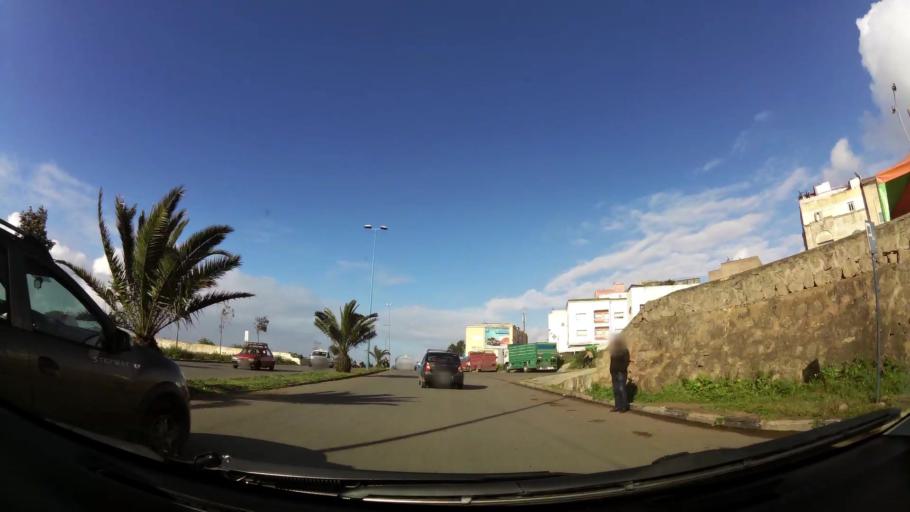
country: MA
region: Grand Casablanca
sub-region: Casablanca
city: Casablanca
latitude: 33.5592
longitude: -7.6867
